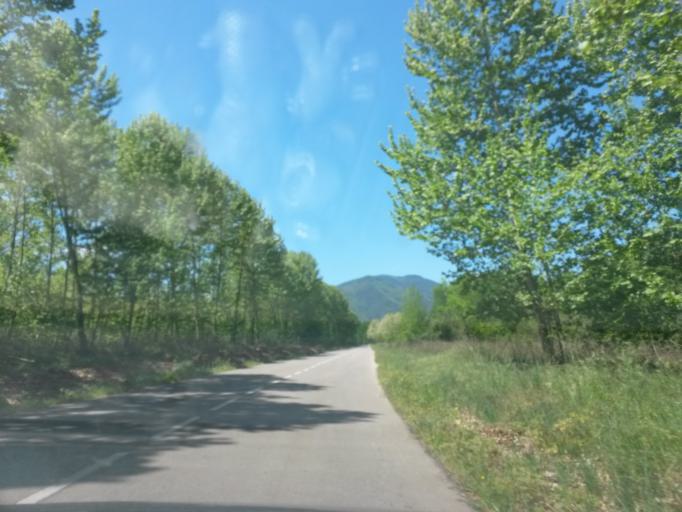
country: ES
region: Catalonia
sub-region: Provincia de Girona
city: Angles
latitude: 41.9633
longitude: 2.6584
